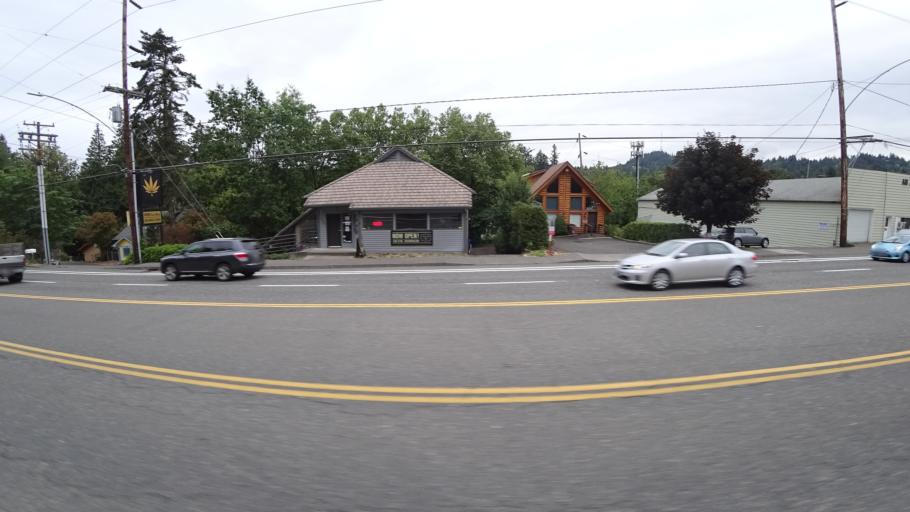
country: US
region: Oregon
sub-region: Washington County
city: Raleigh Hills
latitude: 45.4860
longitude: -122.7252
